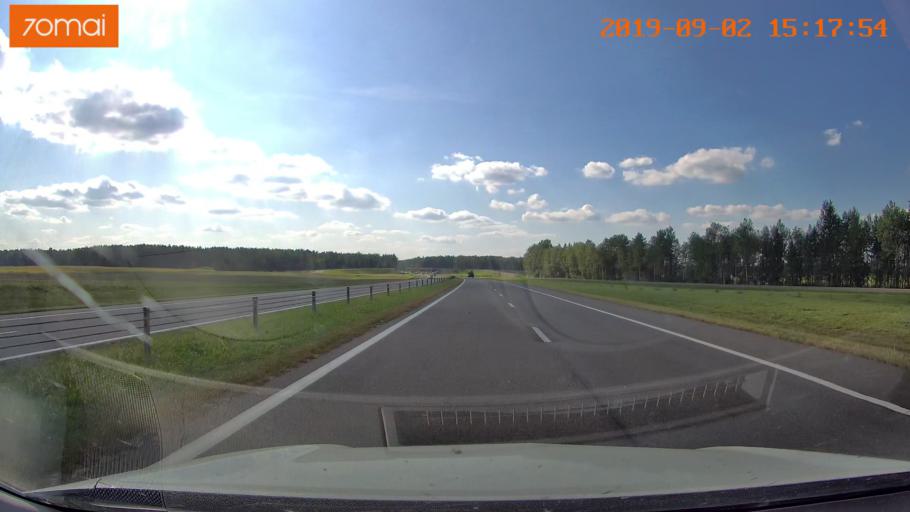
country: BY
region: Mogilev
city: Byalynichy
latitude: 53.9415
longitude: 29.5808
